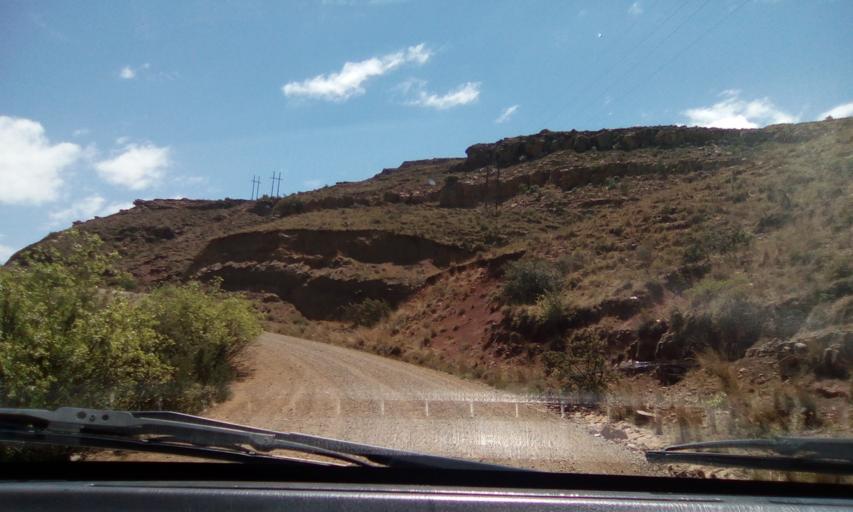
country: LS
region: Qacha's Nek
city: Qacha's Nek
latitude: -30.0671
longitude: 28.6237
